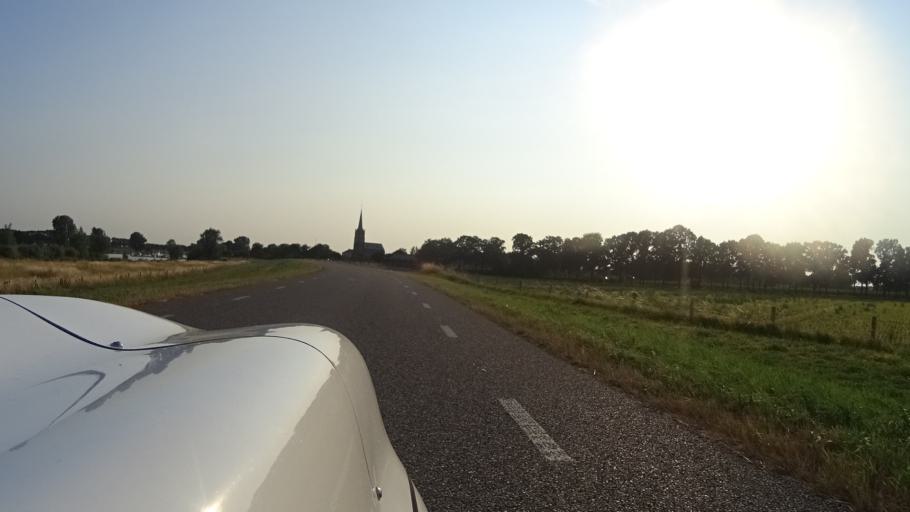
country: NL
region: Gelderland
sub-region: Gemeente Wijchen
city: Bergharen
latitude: 51.8244
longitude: 5.6381
